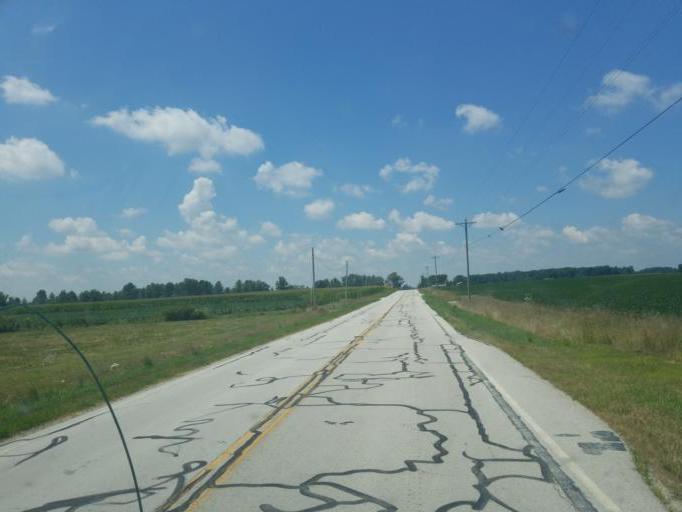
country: US
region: Ohio
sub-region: Allen County
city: Spencerville
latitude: 40.6774
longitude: -84.4572
